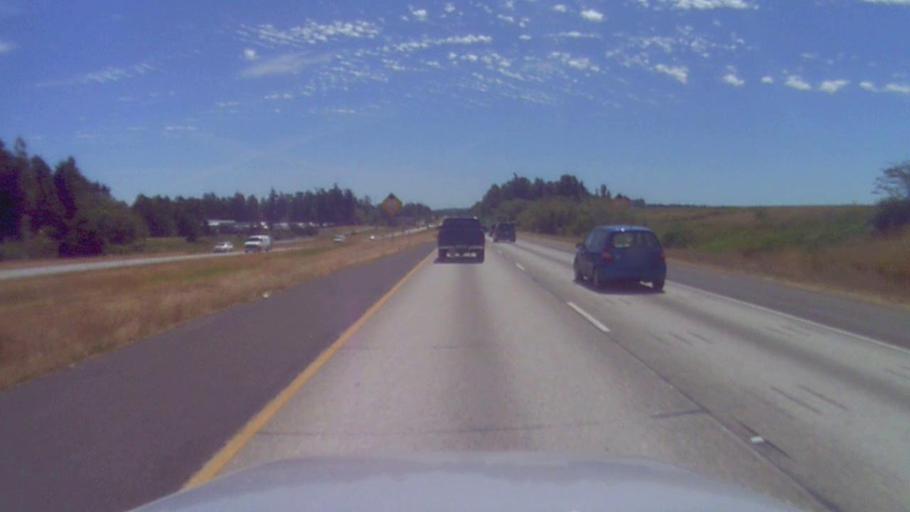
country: US
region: Washington
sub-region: Whatcom County
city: Marietta-Alderwood
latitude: 48.8051
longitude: -122.5367
